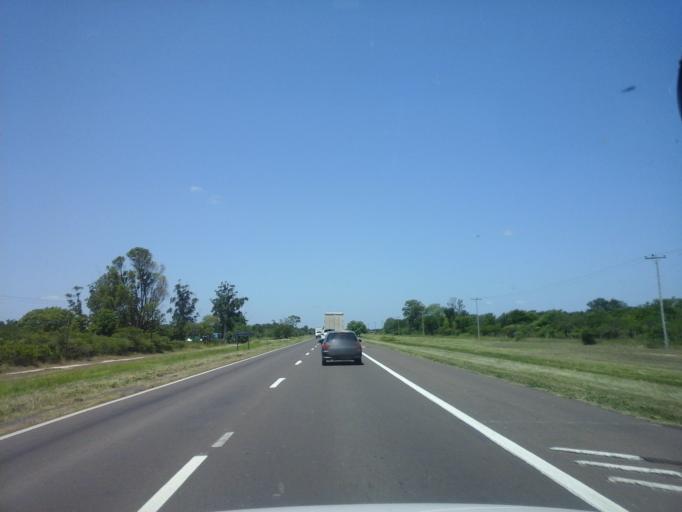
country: AR
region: Corrientes
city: Paso de la Patria
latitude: -27.4076
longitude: -58.6514
